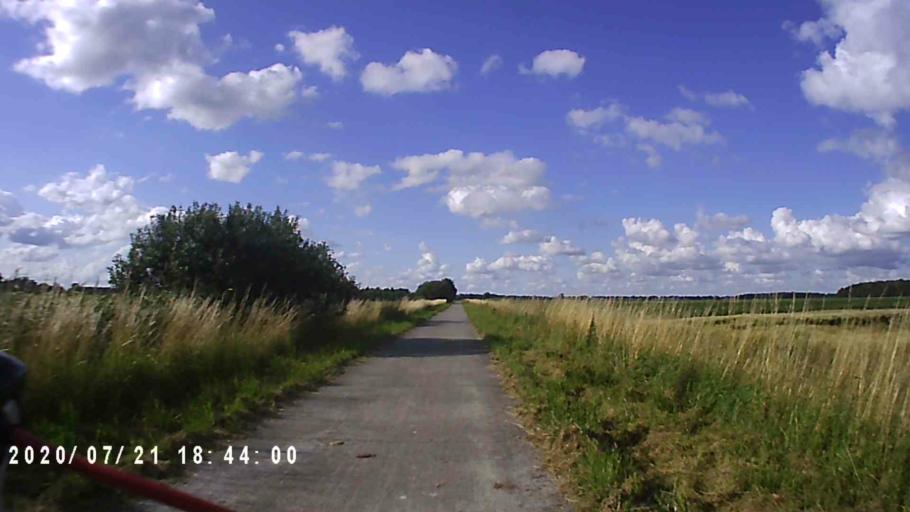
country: NL
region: Groningen
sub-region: Gemeente Hoogezand-Sappemeer
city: Hoogezand
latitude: 53.2045
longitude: 6.7491
